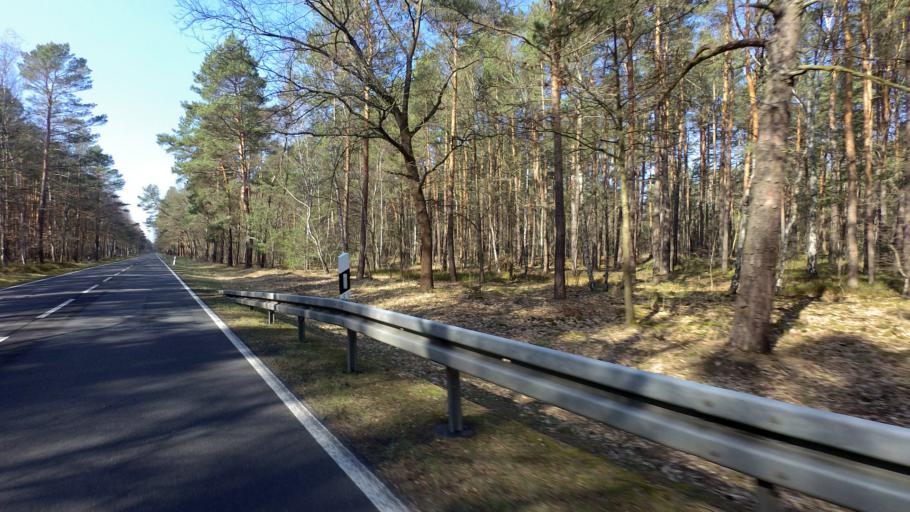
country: DE
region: Brandenburg
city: Sperenberg
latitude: 52.0889
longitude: 13.3436
